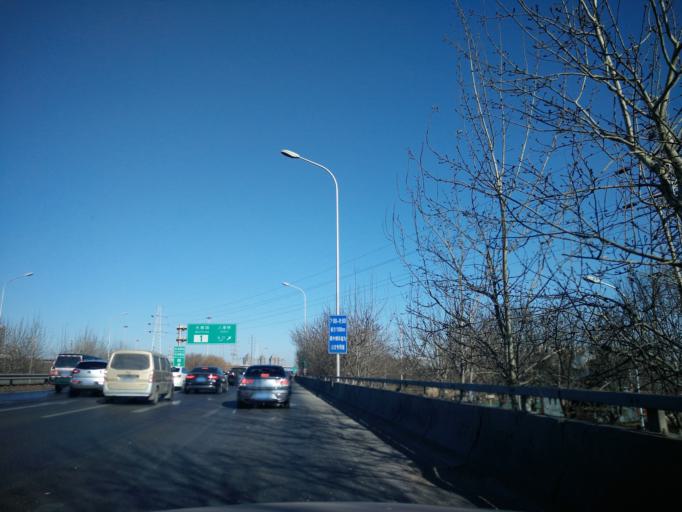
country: CN
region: Beijing
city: Huaxiang
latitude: 39.8441
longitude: 116.3400
